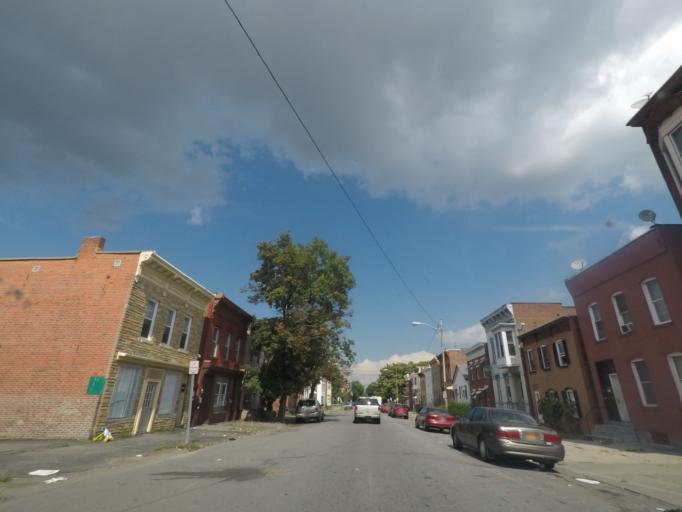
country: US
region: New York
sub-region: Rensselaer County
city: Troy
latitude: 42.7188
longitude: -73.6918
